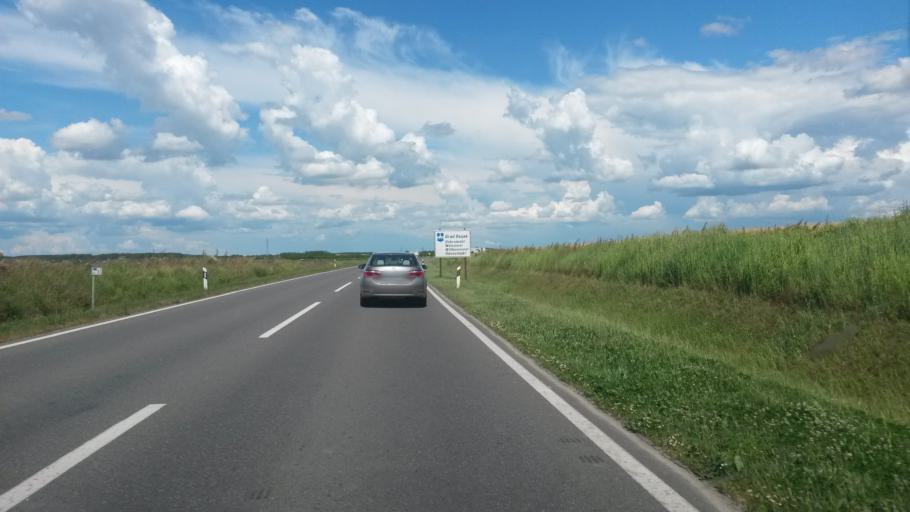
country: HR
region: Osjecko-Baranjska
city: Visnjevac
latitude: 45.5457
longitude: 18.6137
